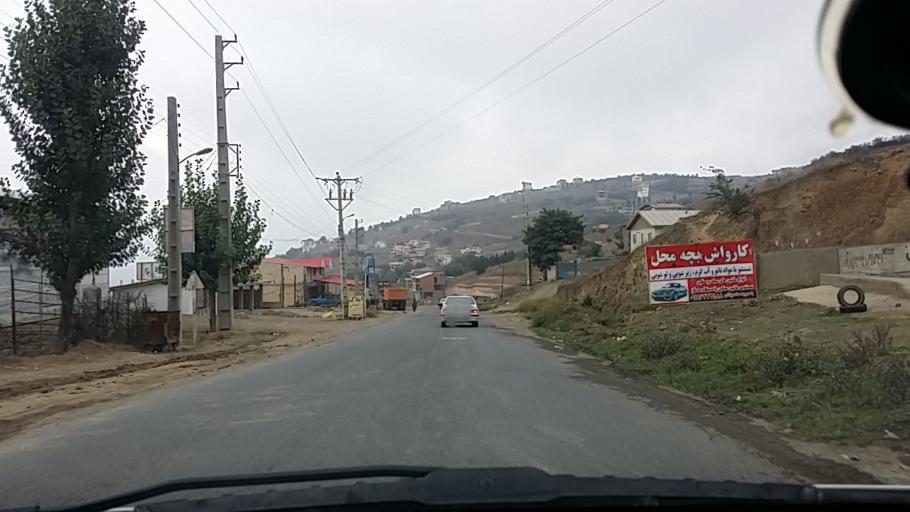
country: IR
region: Mazandaran
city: Chalus
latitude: 36.4887
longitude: 51.2668
